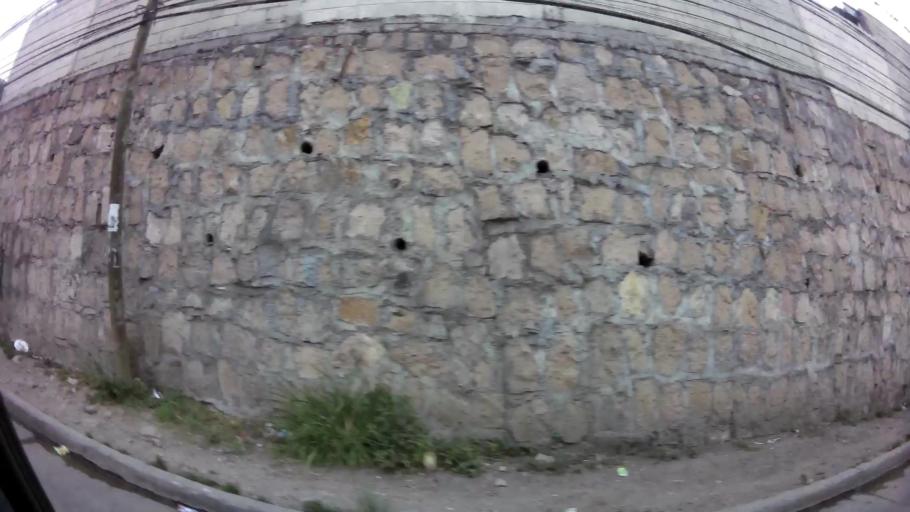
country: HN
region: Francisco Morazan
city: Tegucigalpa
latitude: 14.0709
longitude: -87.2354
